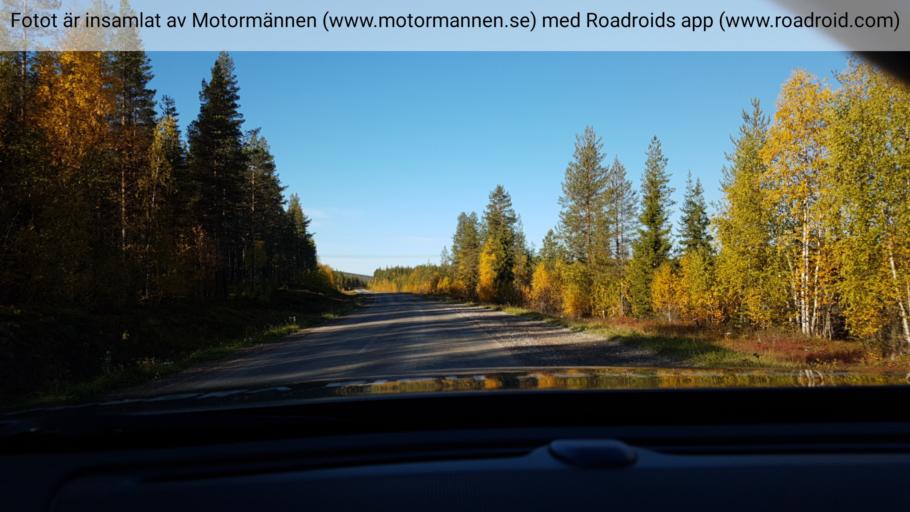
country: SE
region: Norrbotten
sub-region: Alvsbyns Kommun
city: AElvsbyn
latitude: 66.2656
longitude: 21.0603
